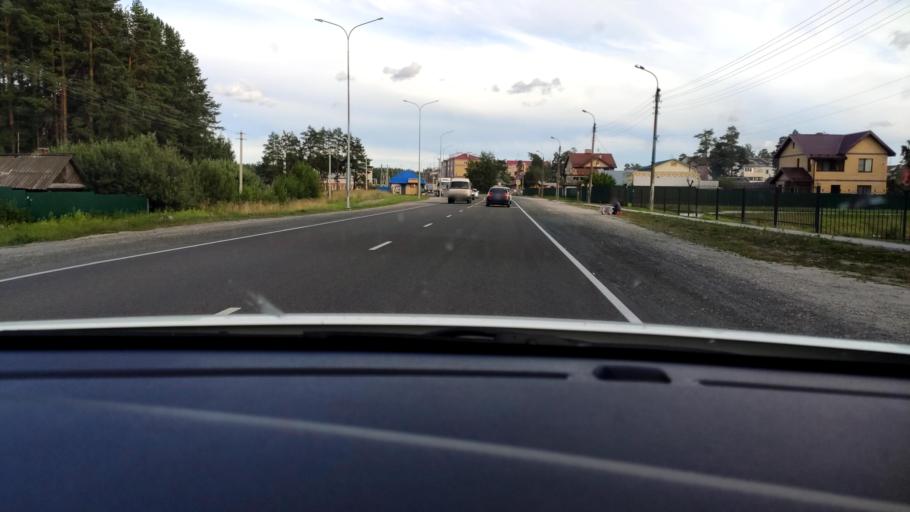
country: RU
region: Mariy-El
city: Suslonger
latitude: 56.3823
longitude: 48.1973
